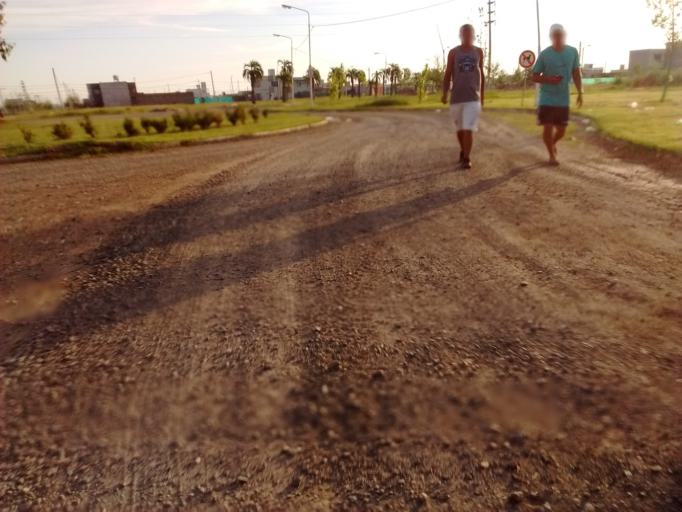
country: AR
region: Santa Fe
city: Roldan
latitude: -32.9350
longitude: -60.8765
